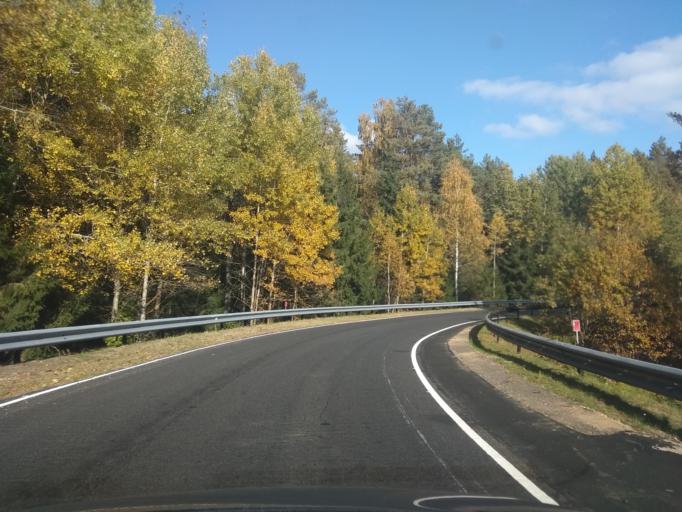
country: BY
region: Brest
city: Baranovichi
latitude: 53.0492
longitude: 25.8431
